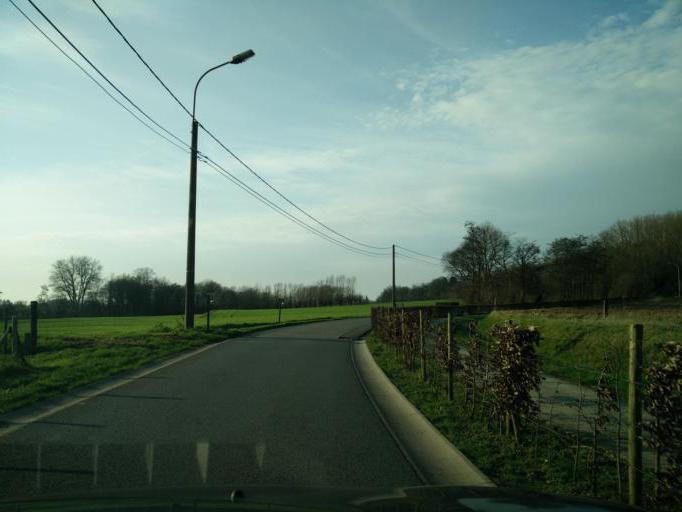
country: BE
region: Flanders
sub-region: Provincie Oost-Vlaanderen
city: Zingem
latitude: 50.8989
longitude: 3.6145
